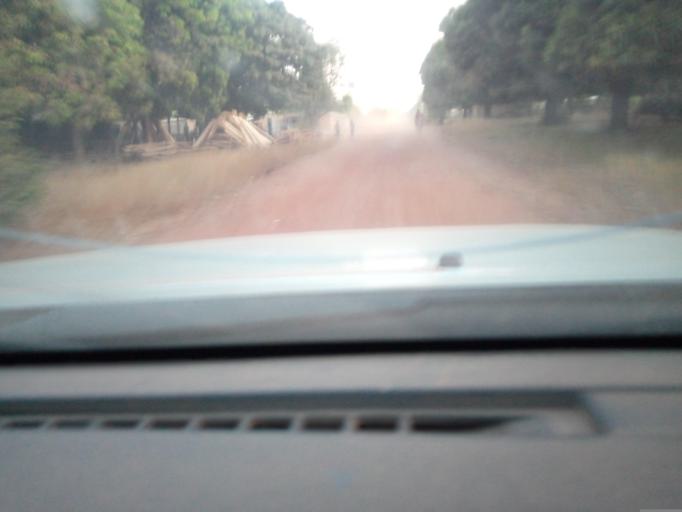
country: ML
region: Sikasso
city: Koutiala
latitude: 12.1001
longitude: -6.1424
